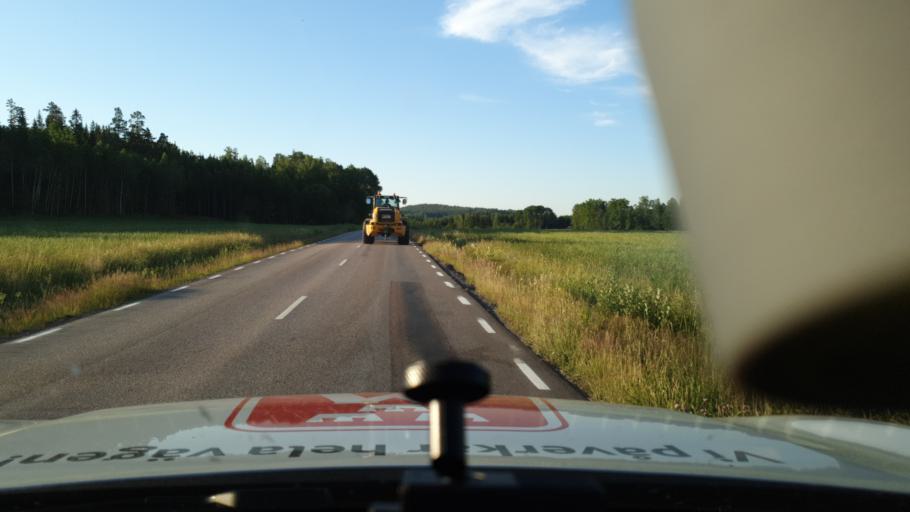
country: SE
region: Vaermland
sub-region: Kils Kommun
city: Kil
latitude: 59.5626
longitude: 13.2901
